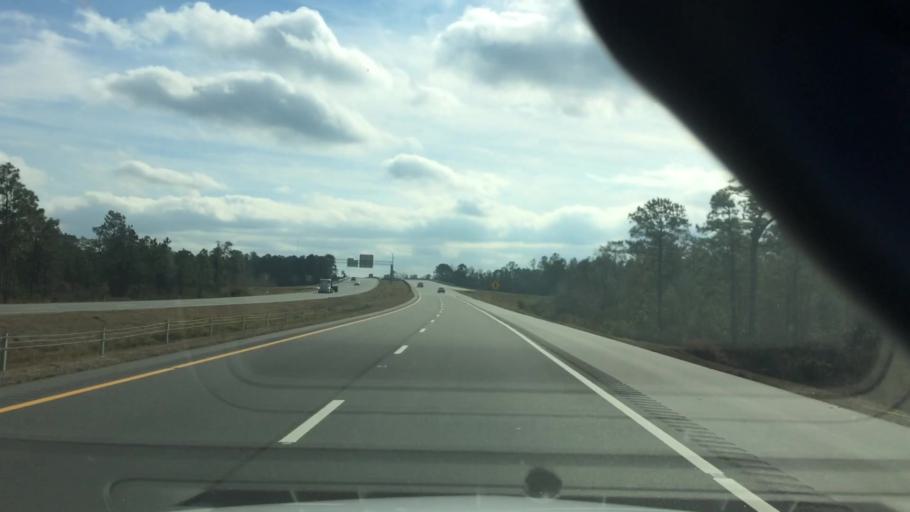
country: US
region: North Carolina
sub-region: Brunswick County
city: Leland
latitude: 34.2622
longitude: -78.0799
